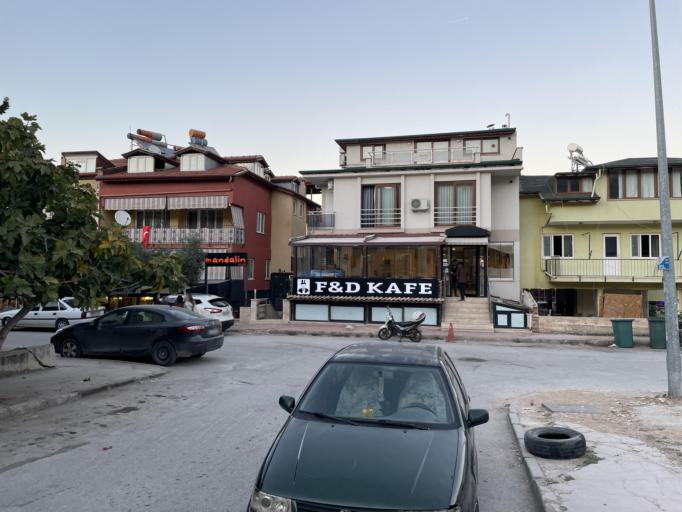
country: TR
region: Denizli
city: Denizli
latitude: 37.7429
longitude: 29.0955
